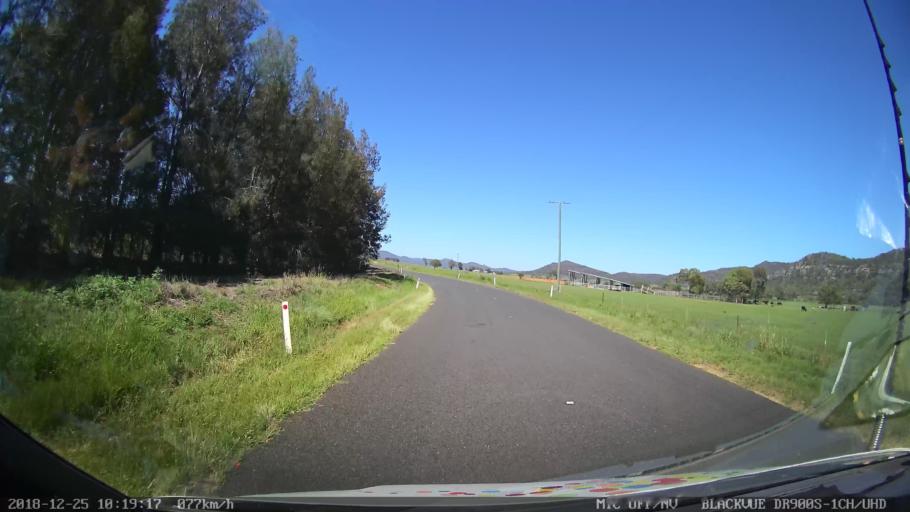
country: AU
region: New South Wales
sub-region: Muswellbrook
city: Denman
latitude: -32.3494
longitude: 150.5597
